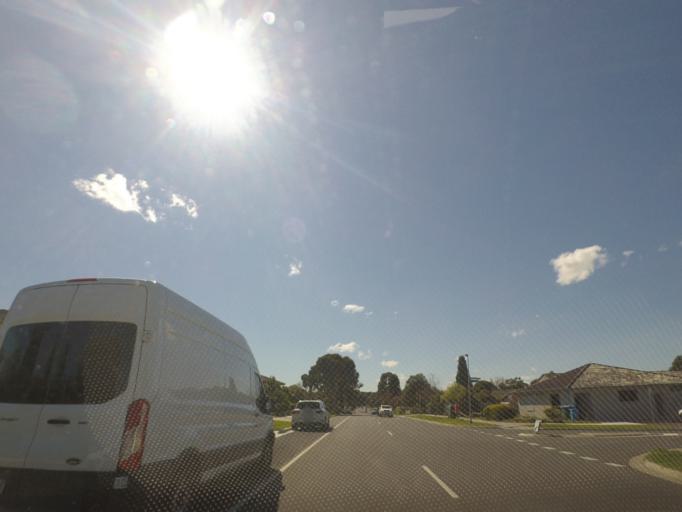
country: AU
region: Victoria
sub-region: Knox
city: Wantirna South
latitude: -37.8679
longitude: 145.2249
